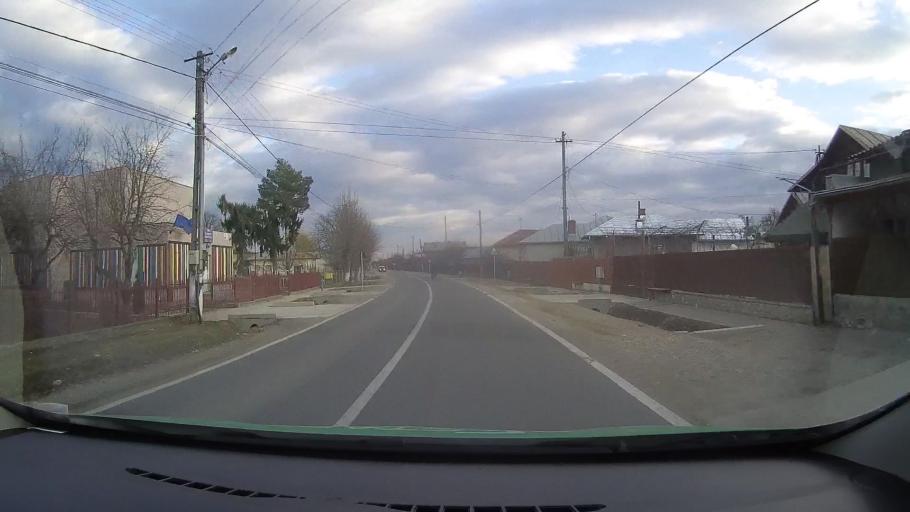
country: RO
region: Dambovita
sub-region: Comuna I. L. Caragiale
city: Ghirdoveni
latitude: 44.9322
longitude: 25.6858
